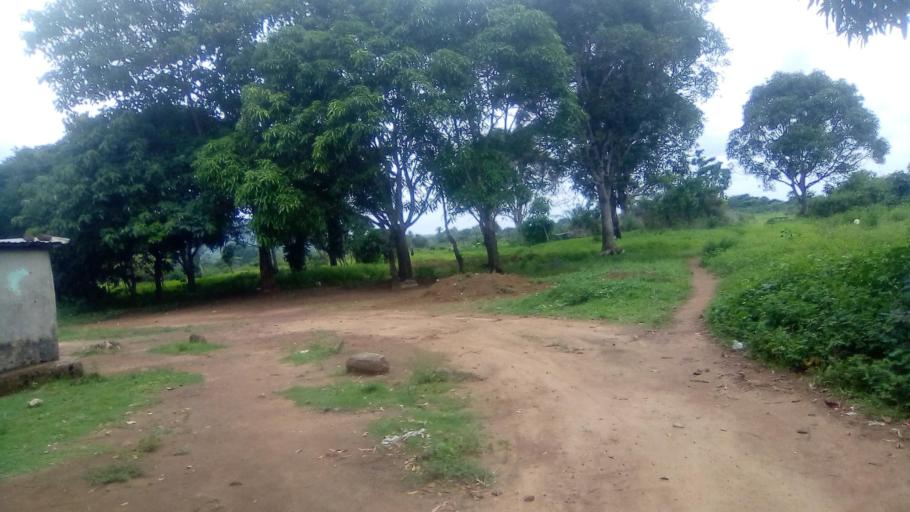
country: SL
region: Southern Province
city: Moyamba
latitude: 8.1573
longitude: -12.4195
